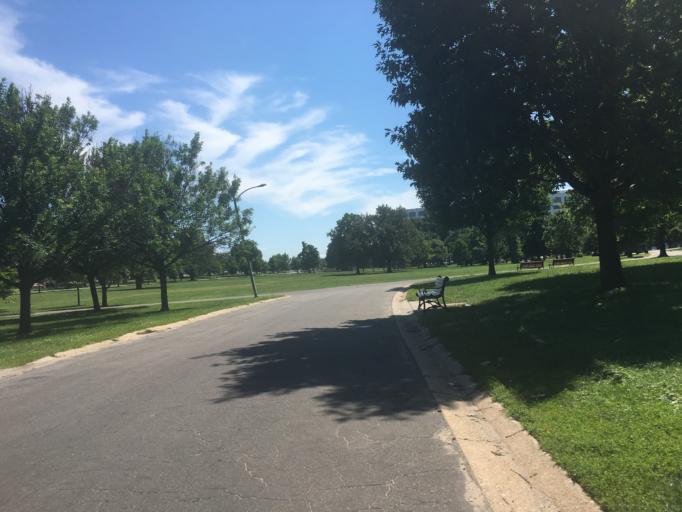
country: US
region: Maryland
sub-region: City of Baltimore
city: Baltimore
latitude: 39.2785
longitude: -76.6410
